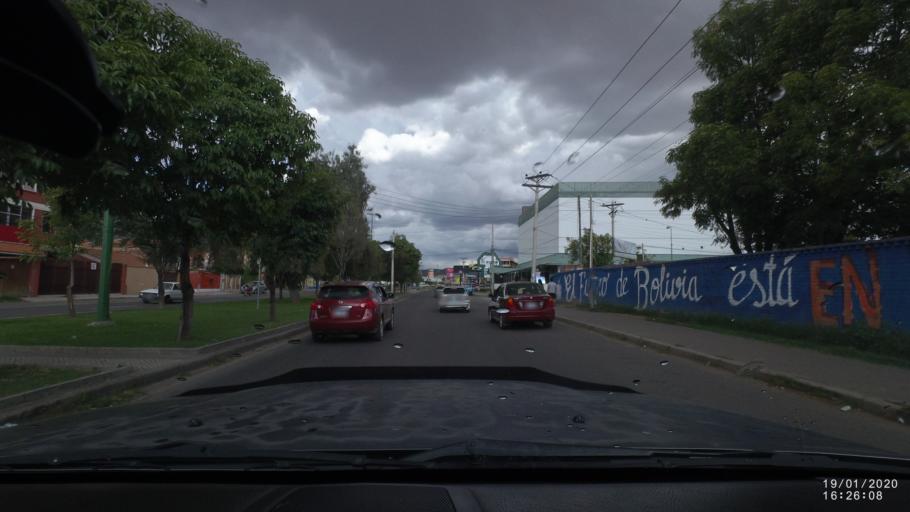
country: BO
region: Cochabamba
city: Cochabamba
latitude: -17.3883
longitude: -66.1804
